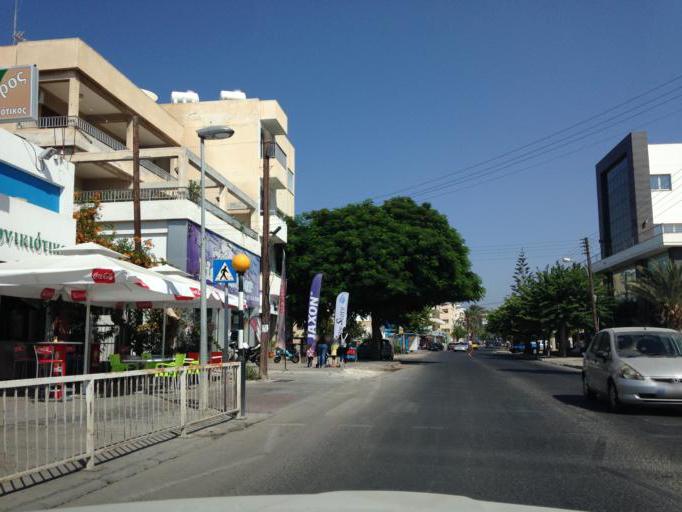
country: CY
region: Pafos
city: Paphos
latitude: 34.7679
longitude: 32.4164
